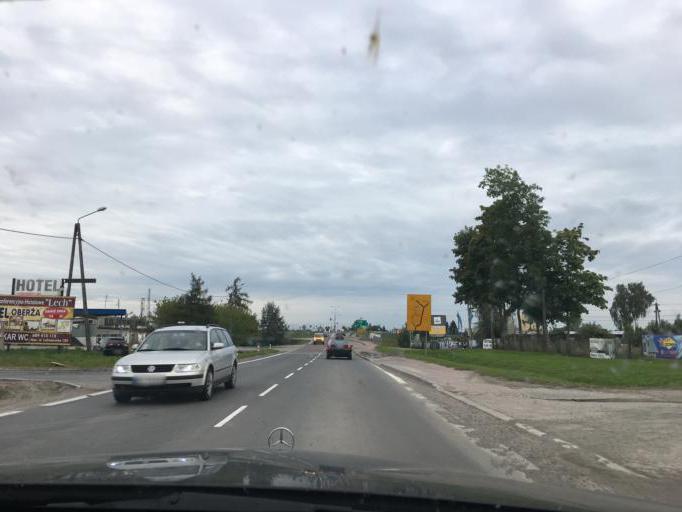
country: PL
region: Masovian Voivodeship
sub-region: Powiat ostrowski
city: Ostrow Mazowiecka
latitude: 52.8212
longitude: 21.8878
